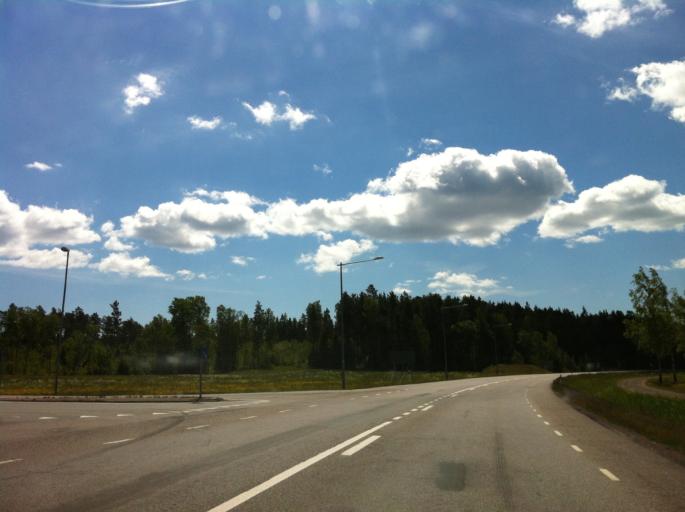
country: SE
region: Vaestra Goetaland
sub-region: Amals Kommun
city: Amal
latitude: 59.0184
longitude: 12.6881
